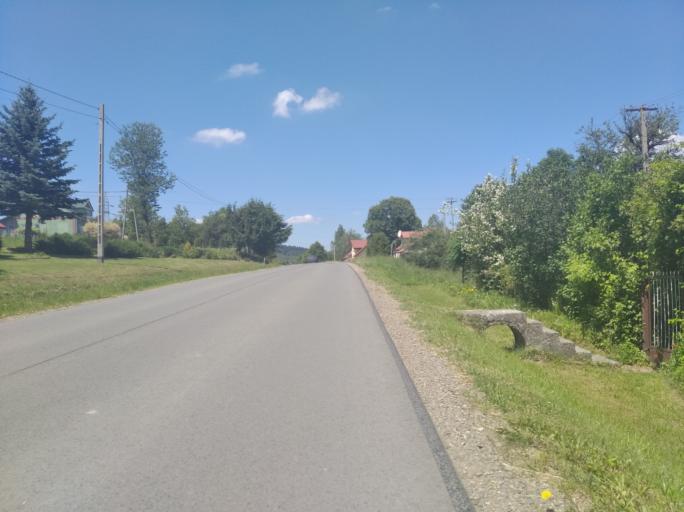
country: PL
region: Subcarpathian Voivodeship
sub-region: Powiat brzozowski
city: Jablonka
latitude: 49.6978
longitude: 22.1346
